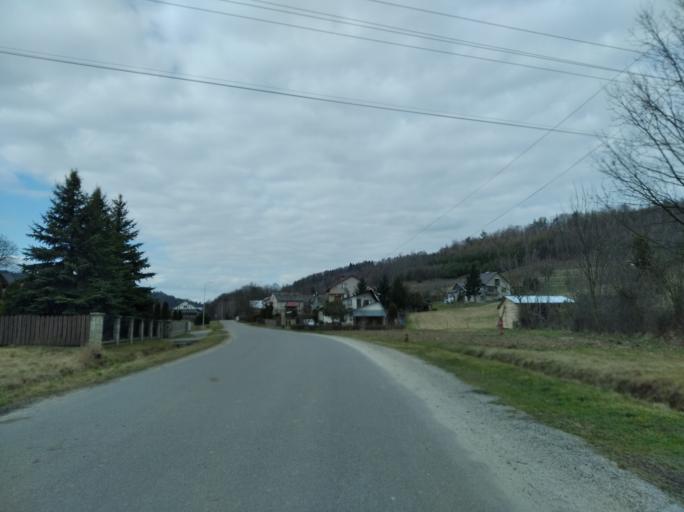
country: PL
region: Subcarpathian Voivodeship
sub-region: Powiat strzyzowski
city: Frysztak
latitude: 49.8448
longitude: 21.6278
